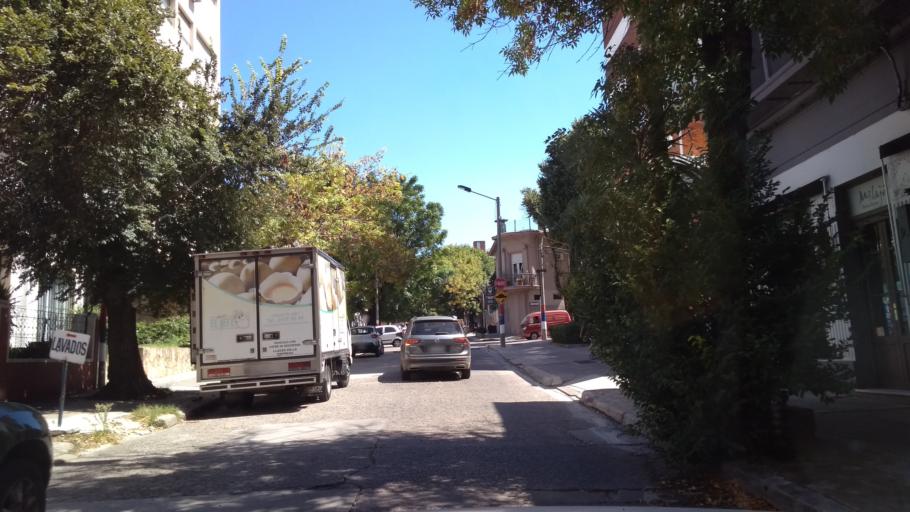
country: UY
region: Montevideo
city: Montevideo
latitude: -34.9071
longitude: -56.1509
